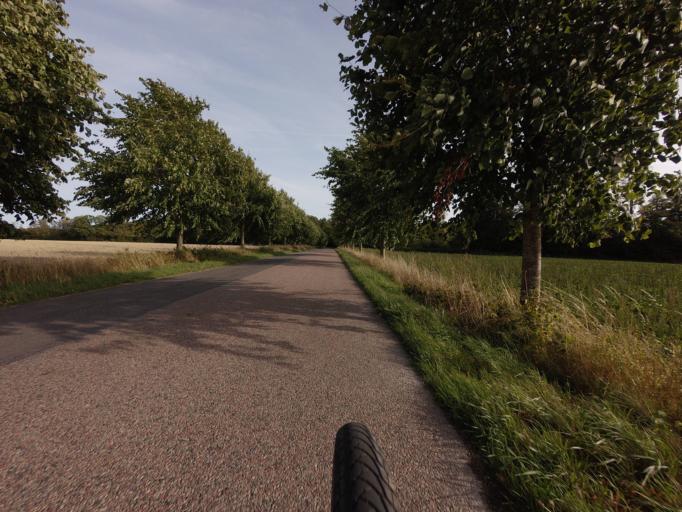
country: DK
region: Zealand
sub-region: Faxe Kommune
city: Fakse Ladeplads
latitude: 55.2447
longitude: 12.2317
